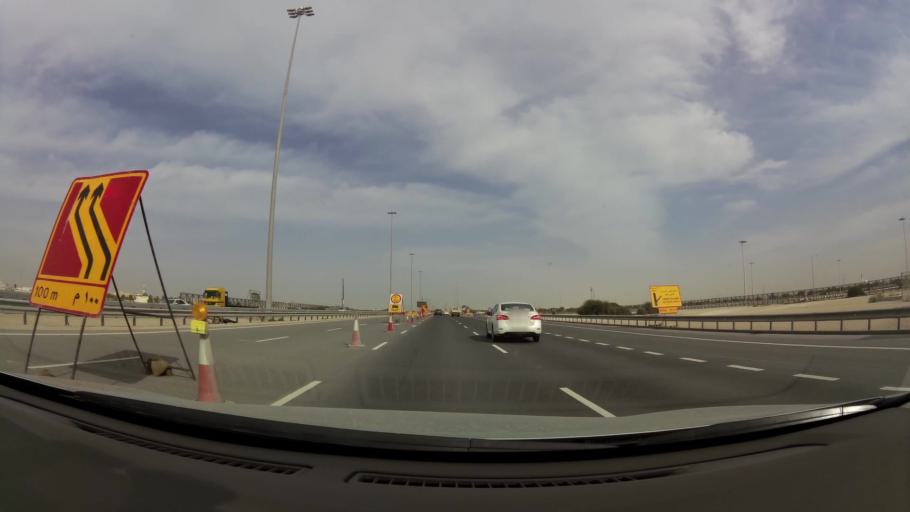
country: QA
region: Baladiyat ar Rayyan
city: Ar Rayyan
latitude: 25.3131
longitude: 51.3804
